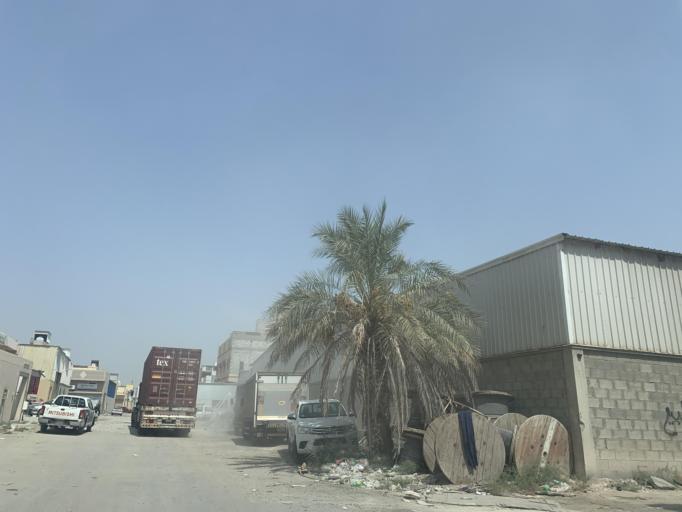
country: BH
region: Central Governorate
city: Madinat Hamad
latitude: 26.1409
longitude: 50.4853
